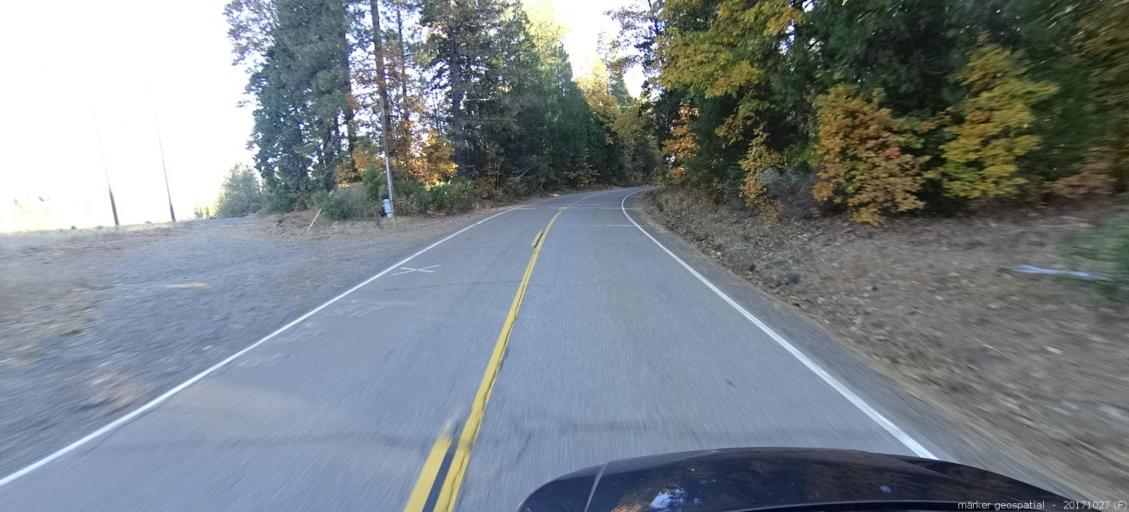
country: US
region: California
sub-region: Shasta County
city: Burney
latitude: 40.9503
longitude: -121.9466
